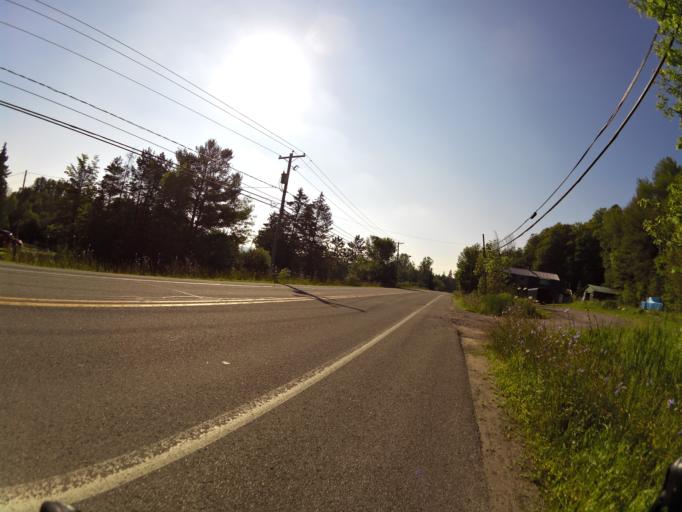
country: CA
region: Quebec
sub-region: Outaouais
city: Wakefield
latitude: 45.5425
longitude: -75.8187
